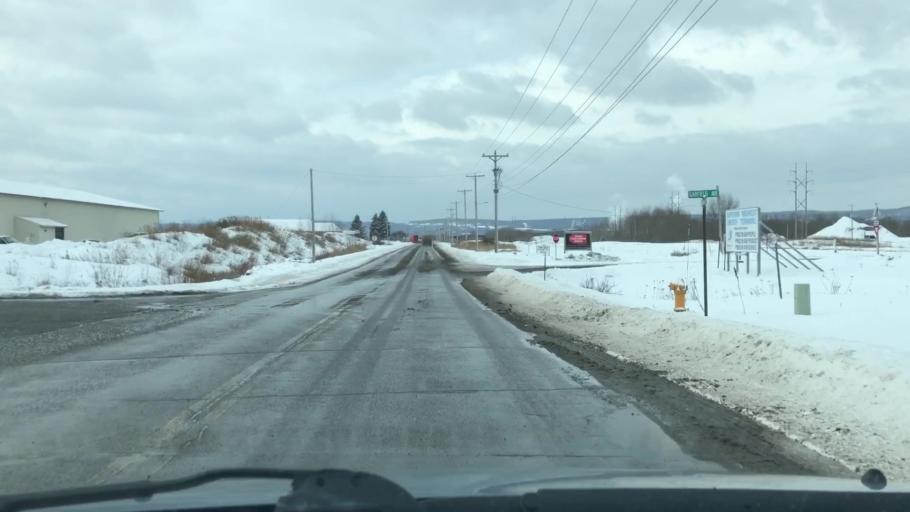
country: US
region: Wisconsin
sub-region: Douglas County
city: Superior
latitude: 46.7281
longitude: -92.1157
